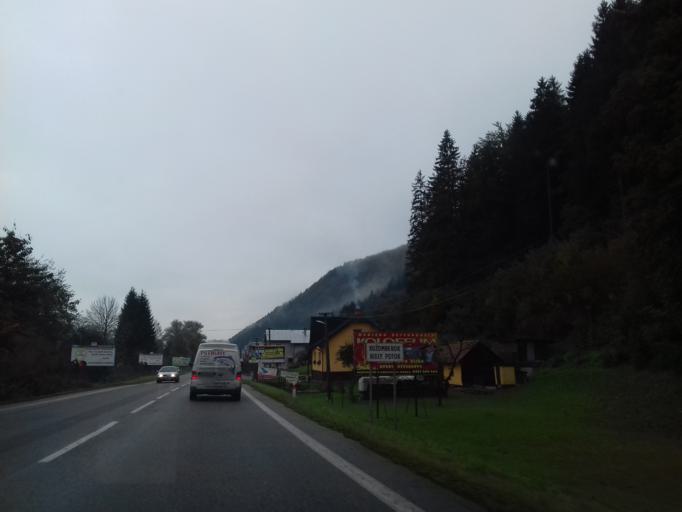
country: SK
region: Zilinsky
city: Ruzomberok
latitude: 49.0238
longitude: 19.2928
